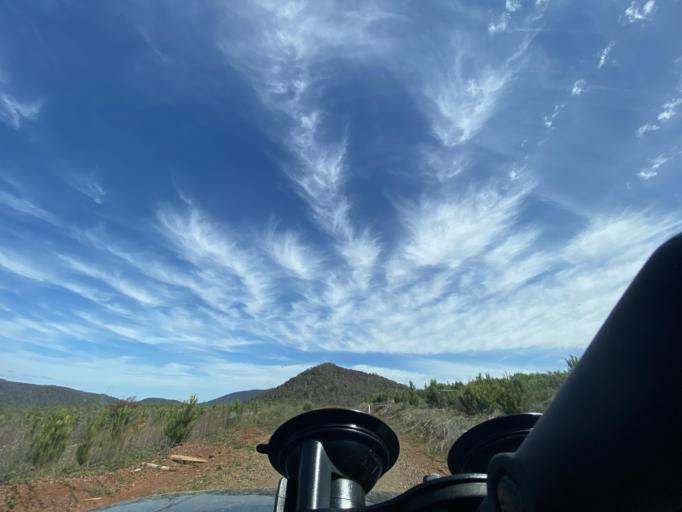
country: AU
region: Victoria
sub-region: Mansfield
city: Mansfield
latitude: -36.8276
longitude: 146.1030
